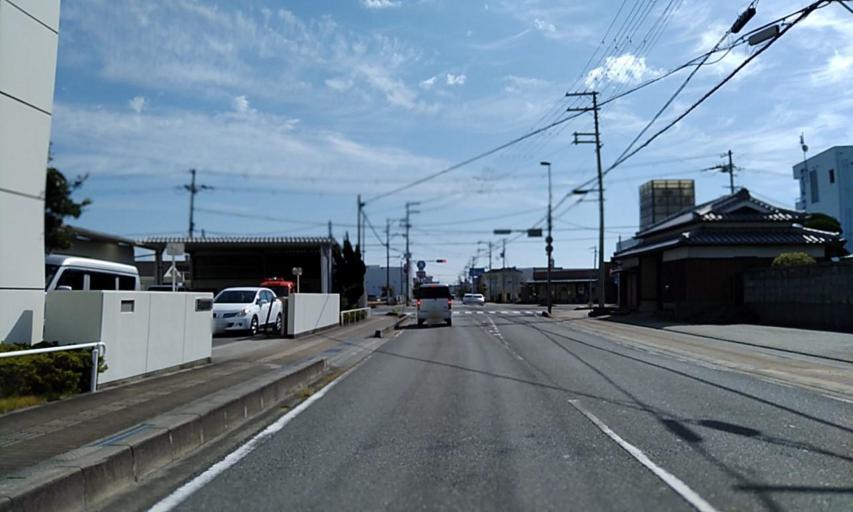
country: JP
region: Wakayama
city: Gobo
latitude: 33.9054
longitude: 135.1517
